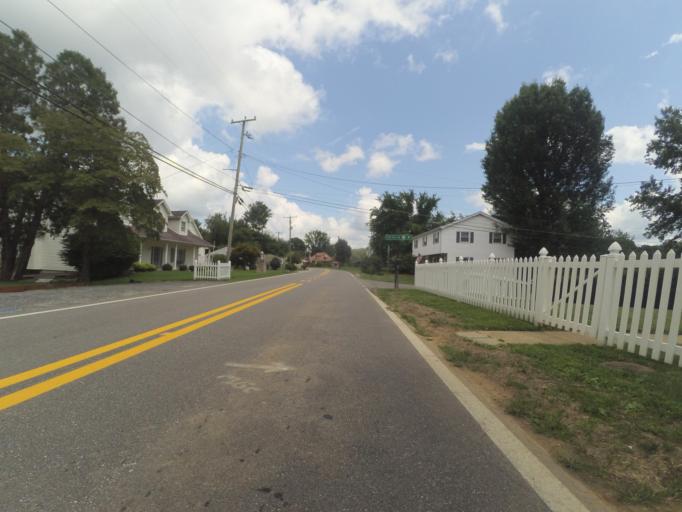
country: US
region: West Virginia
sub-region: Cabell County
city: Pea Ridge
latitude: 38.4095
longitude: -82.3371
